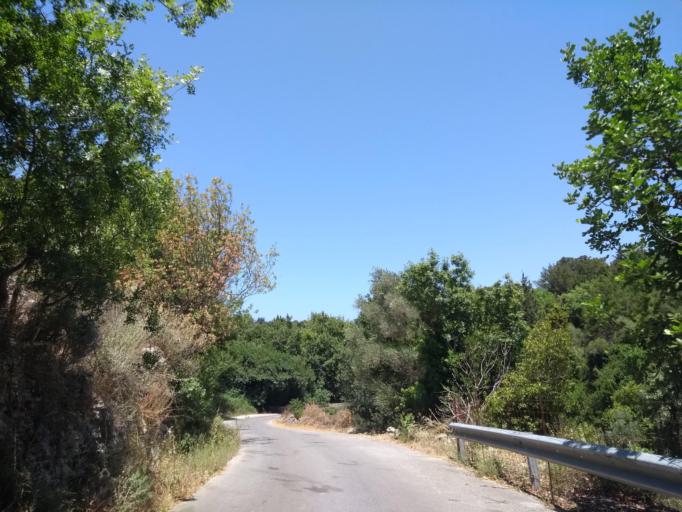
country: GR
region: Crete
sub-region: Nomos Chanias
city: Georgioupolis
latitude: 35.3179
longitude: 24.3068
